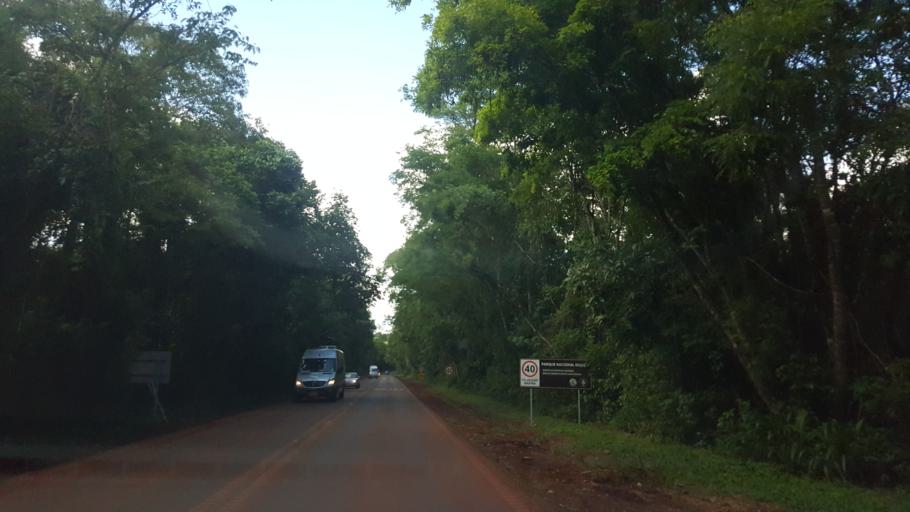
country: AR
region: Misiones
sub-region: Departamento de Iguazu
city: Puerto Iguazu
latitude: -25.7283
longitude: -54.4701
